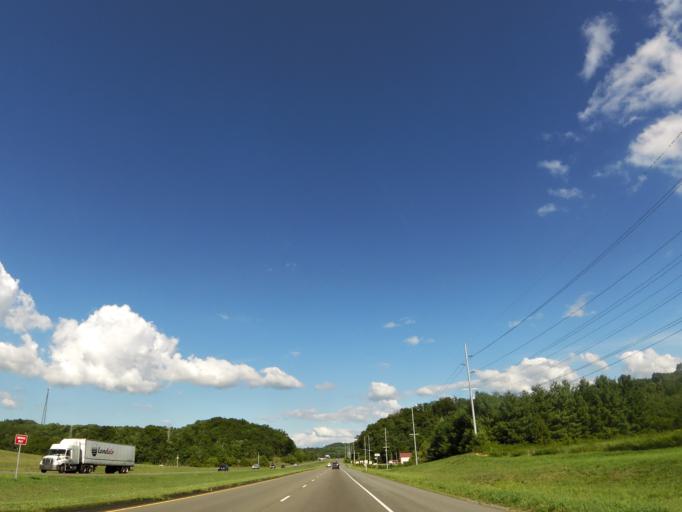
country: US
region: Tennessee
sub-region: Greene County
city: Mosheim
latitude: 36.1726
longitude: -82.8976
